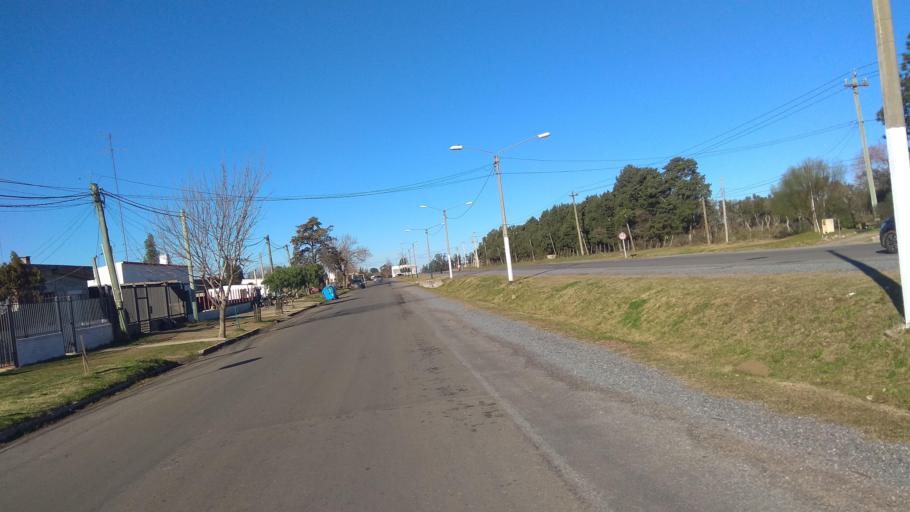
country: UY
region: Florida
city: Florida
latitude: -34.0885
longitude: -56.2378
